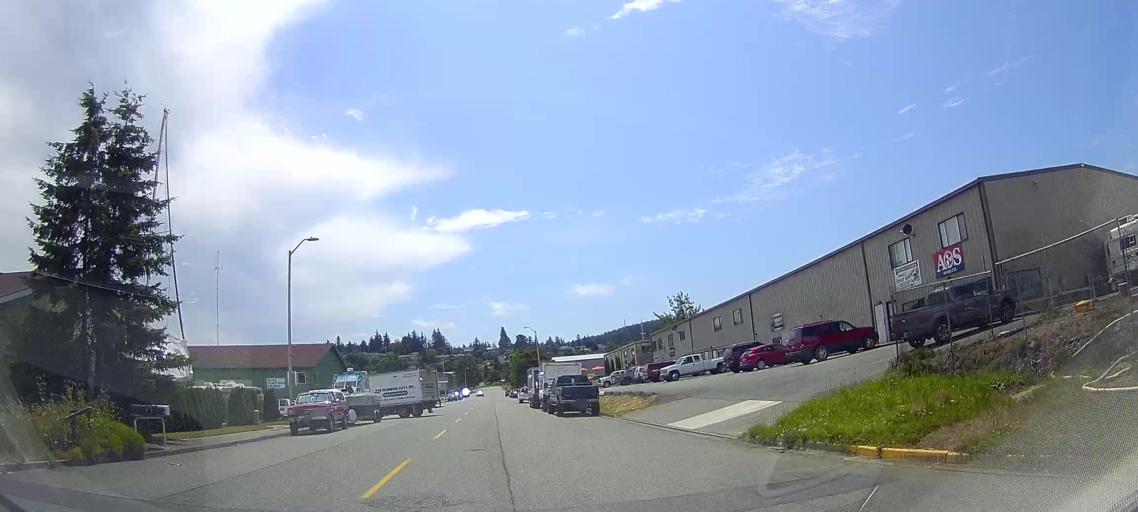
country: US
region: Washington
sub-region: Skagit County
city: Anacortes
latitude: 48.4987
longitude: -122.6067
